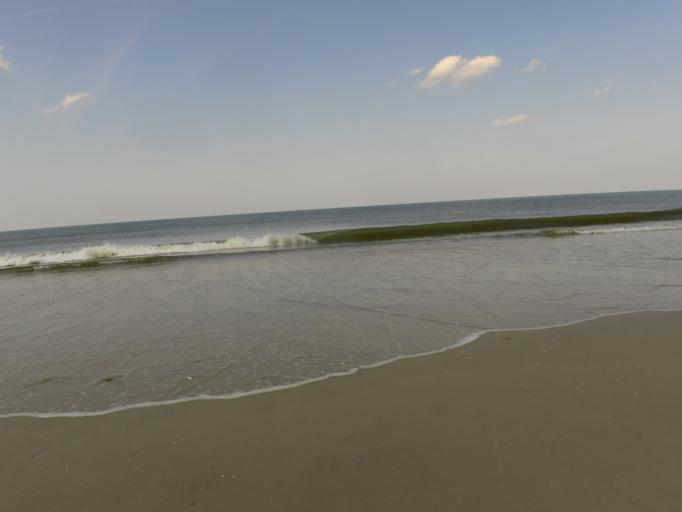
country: US
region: Florida
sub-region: Saint Johns County
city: Palm Valley
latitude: 30.1442
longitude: -81.3508
